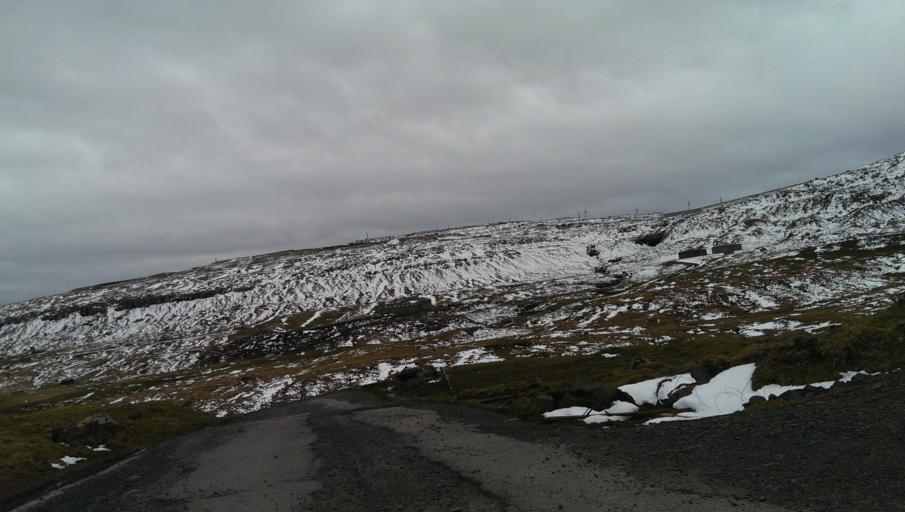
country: FO
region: Streymoy
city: Hoyvik
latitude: 62.0354
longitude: -6.7999
